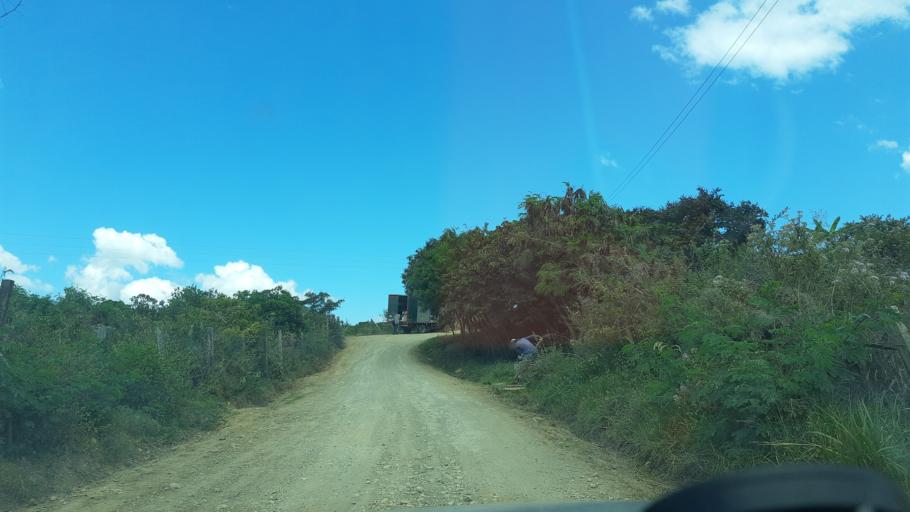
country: CO
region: Boyaca
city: Villa de Leiva
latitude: 5.6681
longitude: -73.5734
